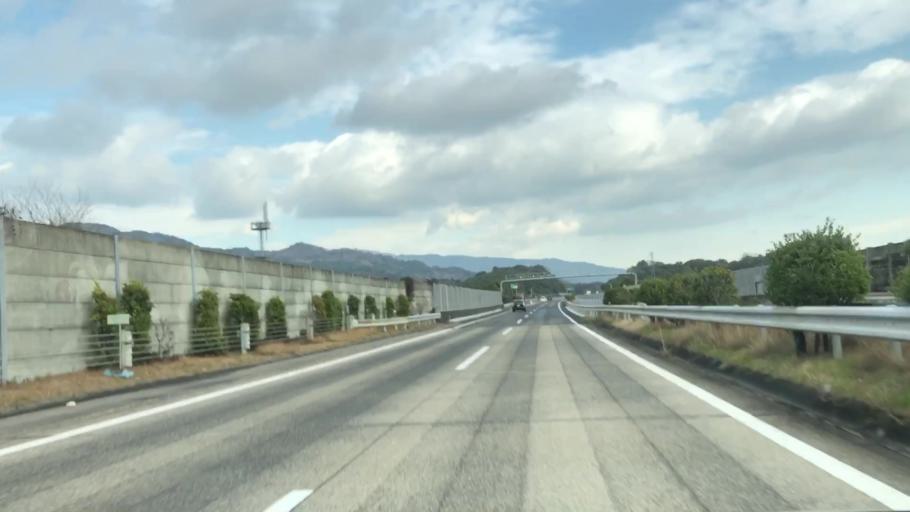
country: JP
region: Saga Prefecture
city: Kanzakimachi-kanzaki
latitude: 33.3463
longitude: 130.3661
